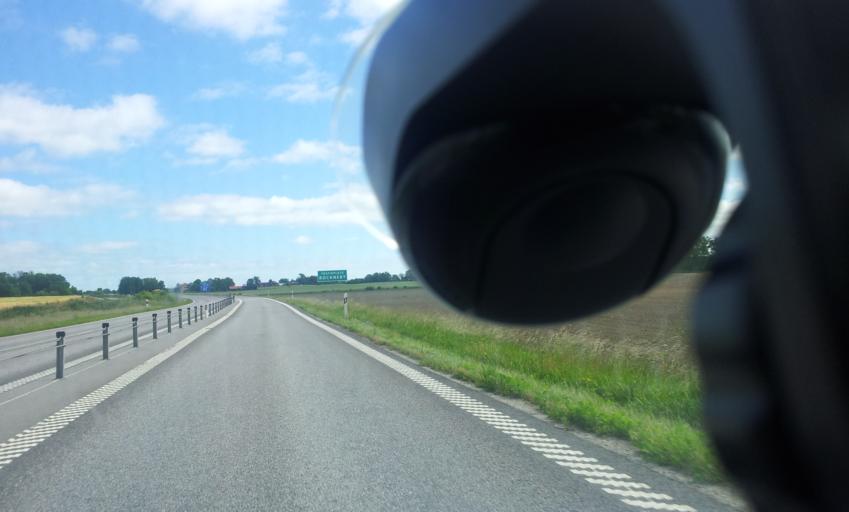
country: SE
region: Kalmar
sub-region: Kalmar Kommun
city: Lindsdal
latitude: 56.7826
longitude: 16.3407
